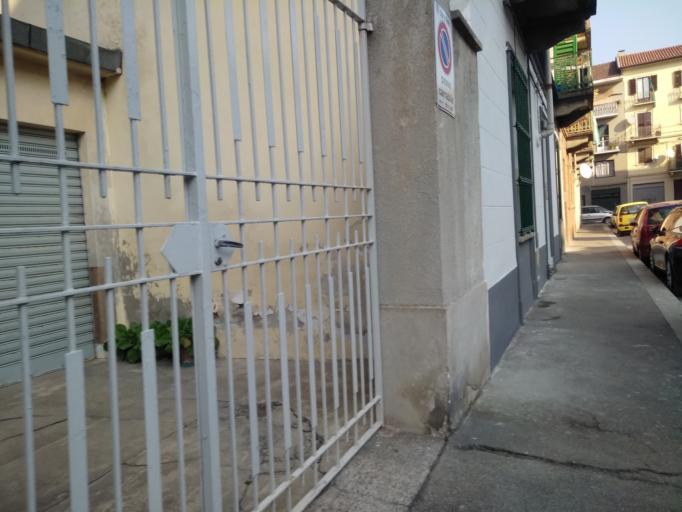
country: IT
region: Piedmont
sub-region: Provincia di Torino
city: Turin
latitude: 45.0899
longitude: 7.6908
